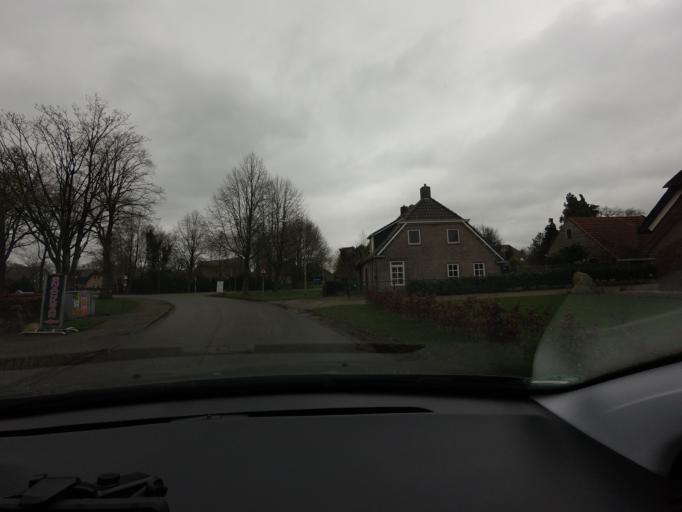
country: NL
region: Drenthe
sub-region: Gemeente Hoogeveen
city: Hoogeveen
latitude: 52.8176
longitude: 6.5167
